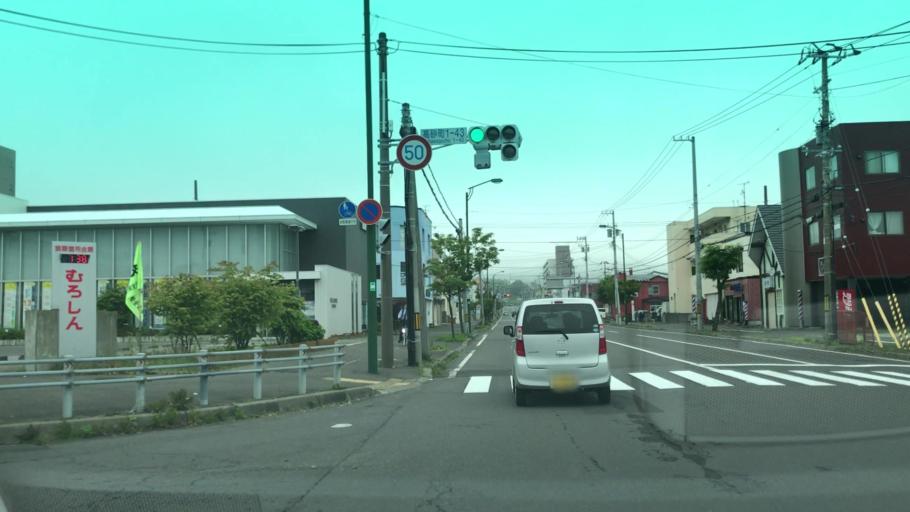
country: JP
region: Hokkaido
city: Muroran
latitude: 42.3607
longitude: 141.0415
